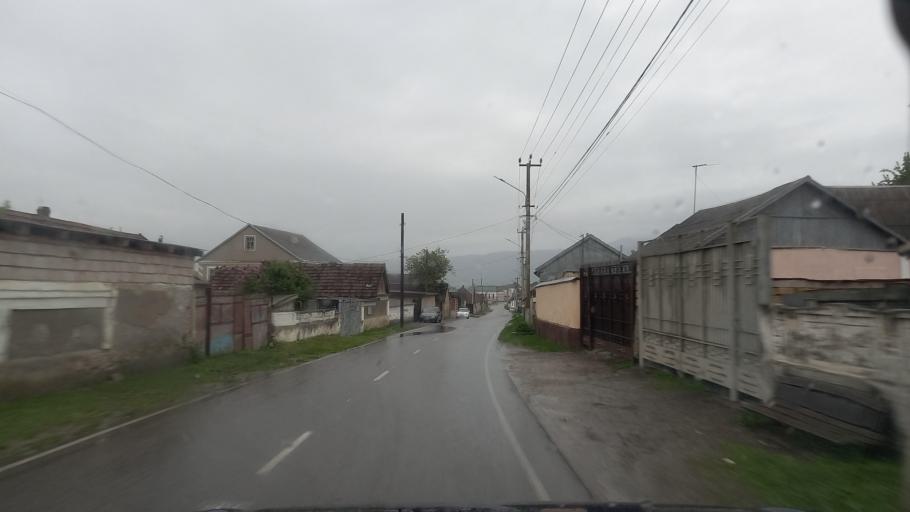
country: RU
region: Kabardino-Balkariya
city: Gundelen
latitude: 43.5947
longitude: 43.1781
